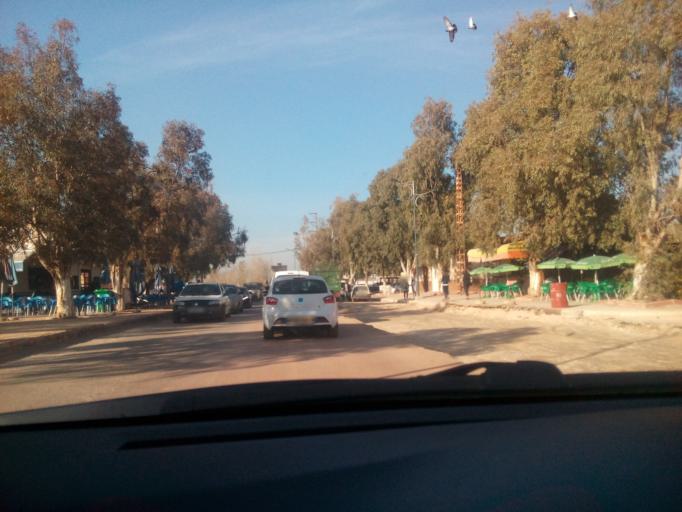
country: DZ
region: Oran
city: Es Senia
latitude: 35.6511
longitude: -0.6128
